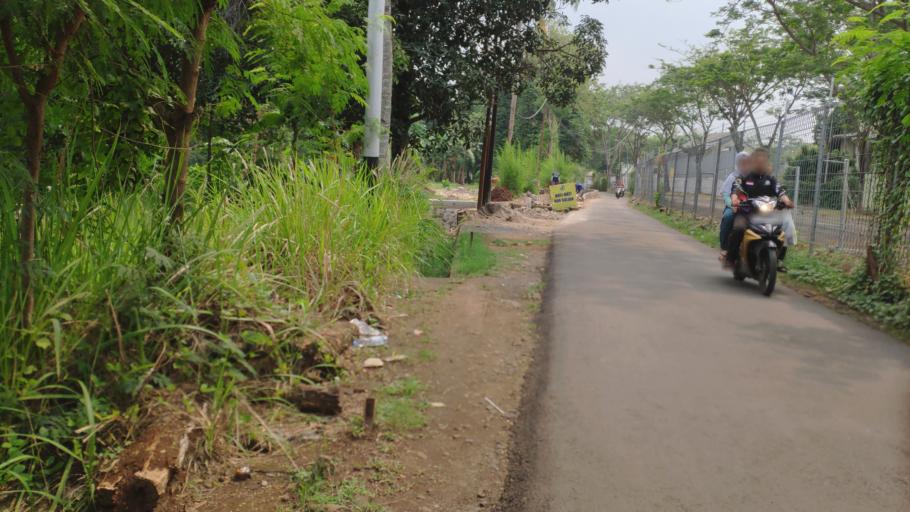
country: ID
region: West Java
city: Depok
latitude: -6.3393
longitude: 106.8174
